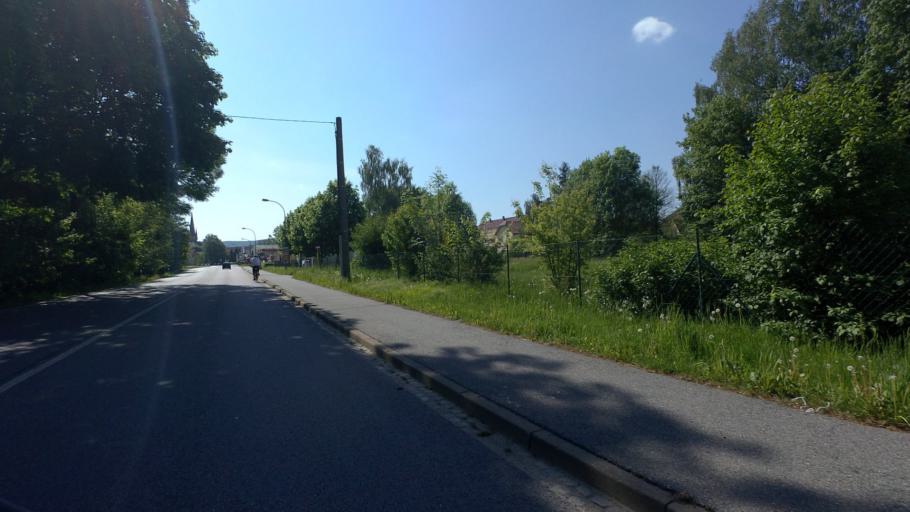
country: DE
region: Saxony
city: Neustadt in Sachsen
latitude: 51.0298
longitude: 14.2071
